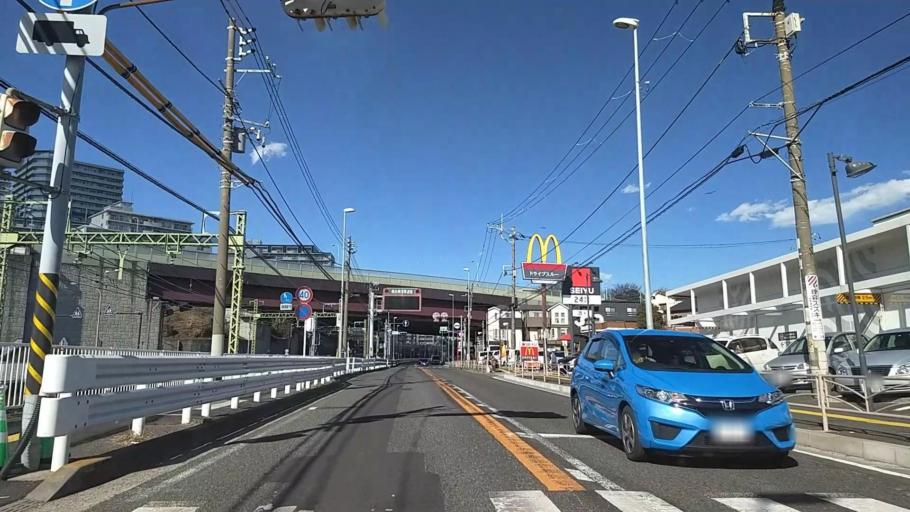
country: JP
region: Kanagawa
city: Zushi
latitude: 35.3549
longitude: 139.6281
